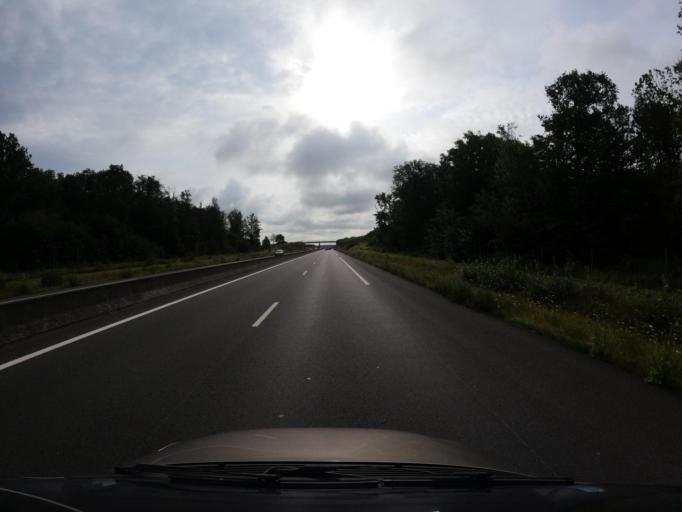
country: FR
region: Centre
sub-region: Departement d'Indre-et-Loire
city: Monts
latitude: 47.3075
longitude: 0.6133
